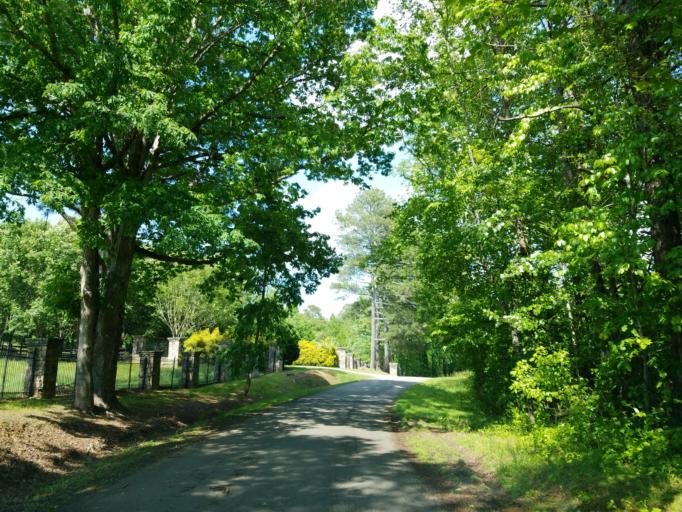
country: US
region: Georgia
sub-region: Cherokee County
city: Ball Ground
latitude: 34.2865
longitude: -84.3090
